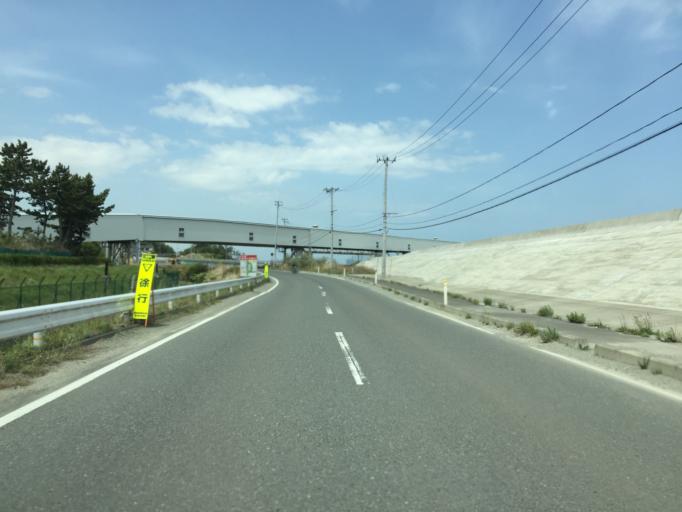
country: JP
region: Miyagi
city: Marumori
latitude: 37.8504
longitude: 140.9470
